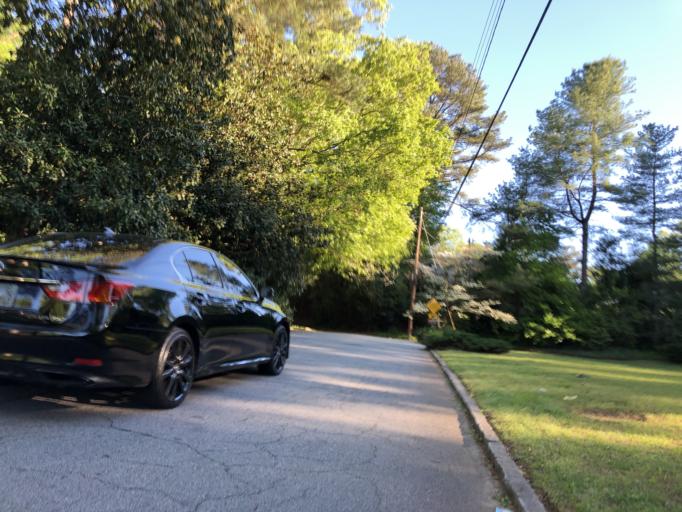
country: US
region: Georgia
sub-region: DeKalb County
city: North Decatur
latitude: 33.7881
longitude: -84.3014
